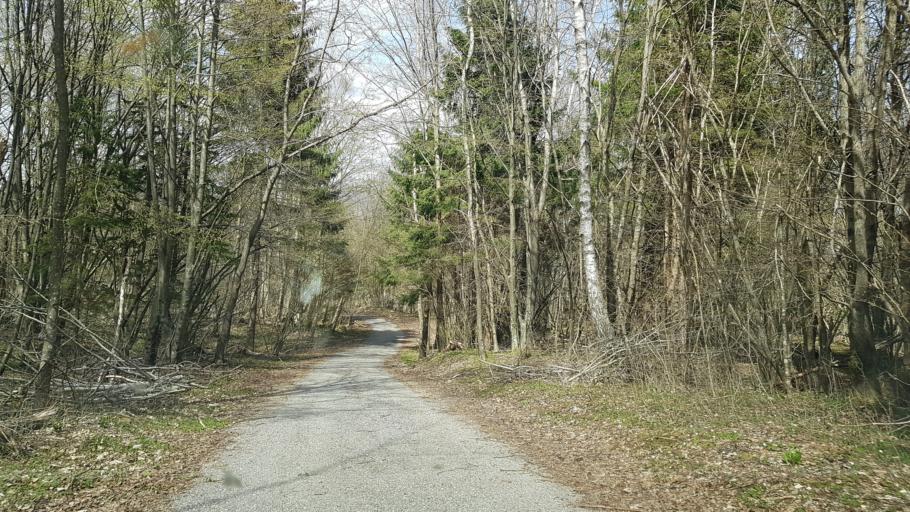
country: IT
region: Friuli Venezia Giulia
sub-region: Provincia di Udine
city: Trasaghis
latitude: 46.2847
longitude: 13.0146
